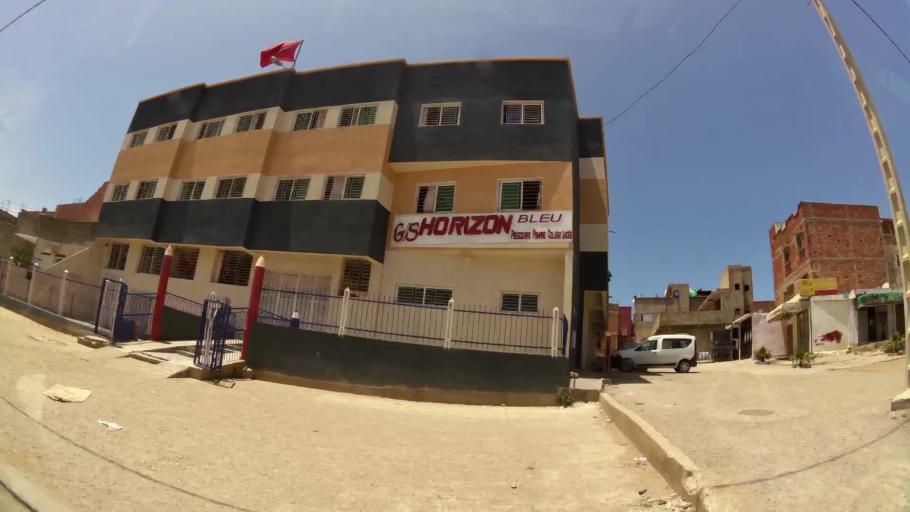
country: MA
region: Gharb-Chrarda-Beni Hssen
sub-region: Kenitra Province
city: Kenitra
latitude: 34.2645
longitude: -6.6434
